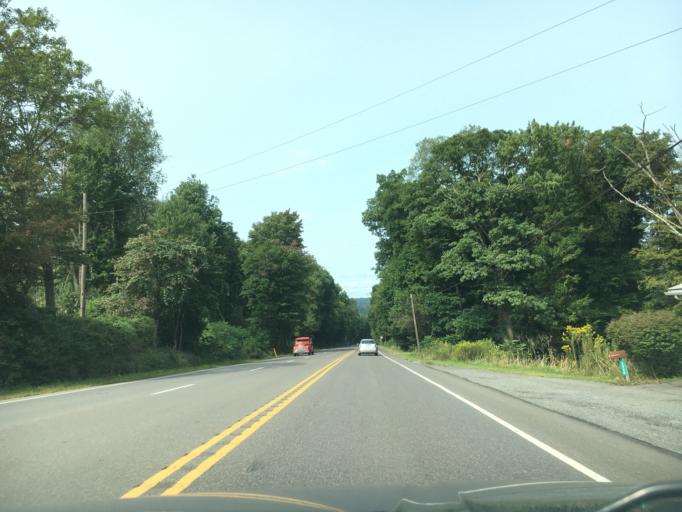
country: US
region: Pennsylvania
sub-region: Carbon County
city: Summit Hill
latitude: 40.7123
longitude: -75.8357
